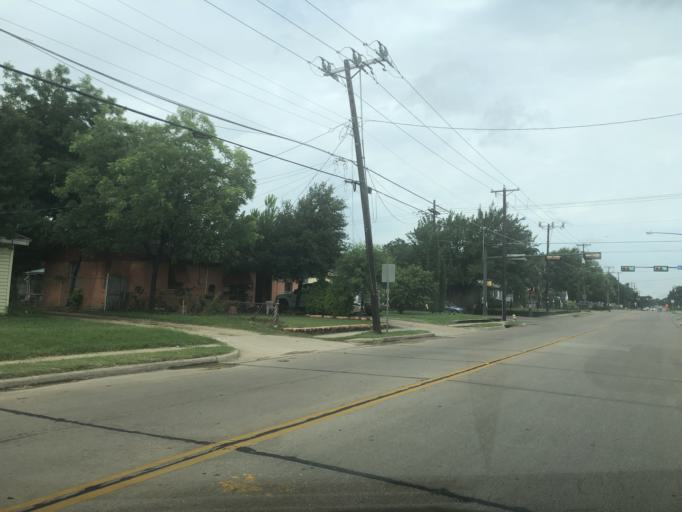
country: US
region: Texas
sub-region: Dallas County
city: Irving
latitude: 32.8086
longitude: -96.9463
